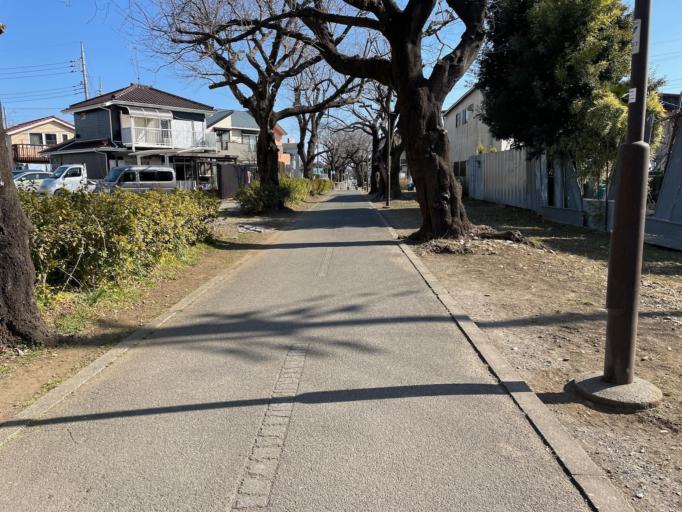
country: JP
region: Tokyo
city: Fussa
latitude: 35.7556
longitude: 139.3647
